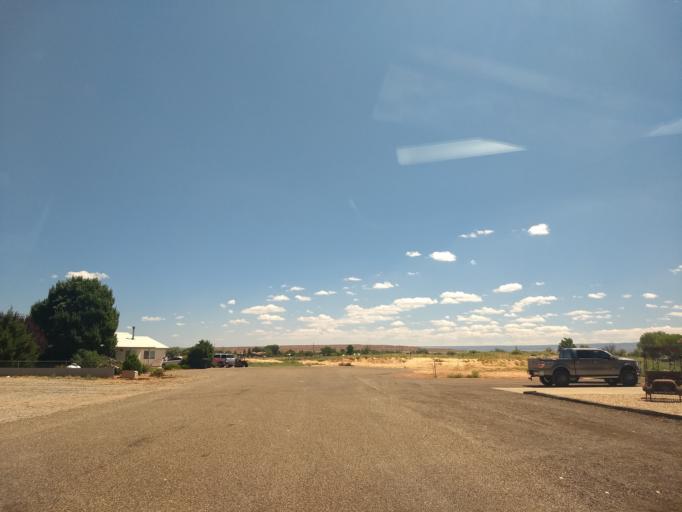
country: US
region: Arizona
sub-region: Coconino County
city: Fredonia
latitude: 36.9411
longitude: -112.5347
